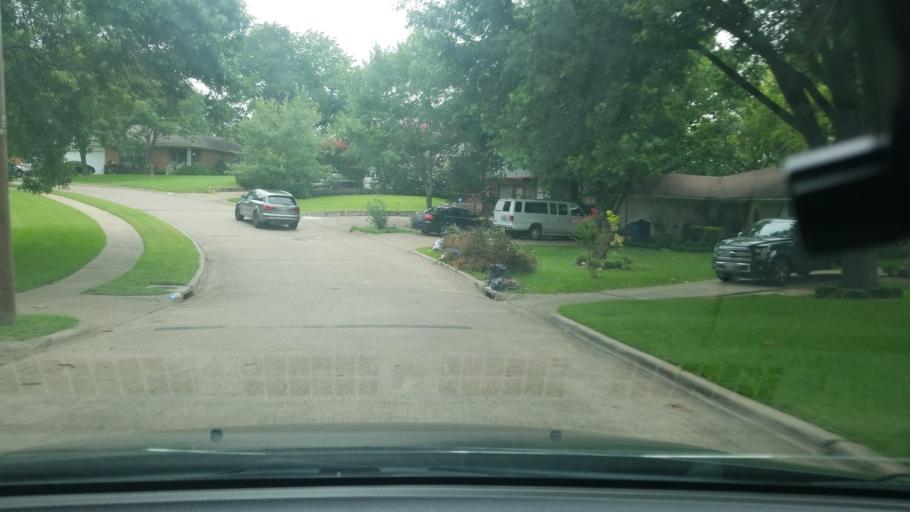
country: US
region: Texas
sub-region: Dallas County
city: Balch Springs
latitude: 32.7689
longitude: -96.6919
